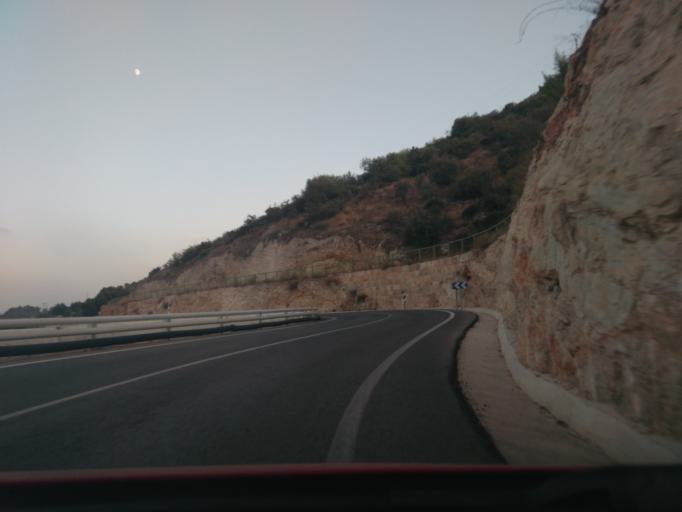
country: ES
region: Valencia
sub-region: Provincia de Valencia
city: Sumacarcer
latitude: 39.0901
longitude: -0.6264
